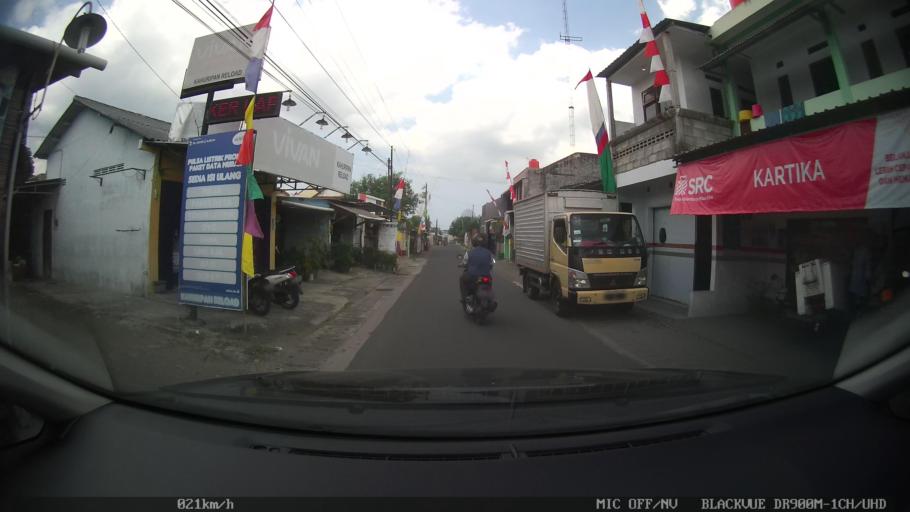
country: ID
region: Daerah Istimewa Yogyakarta
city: Gamping Lor
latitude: -7.8096
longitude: 110.3280
